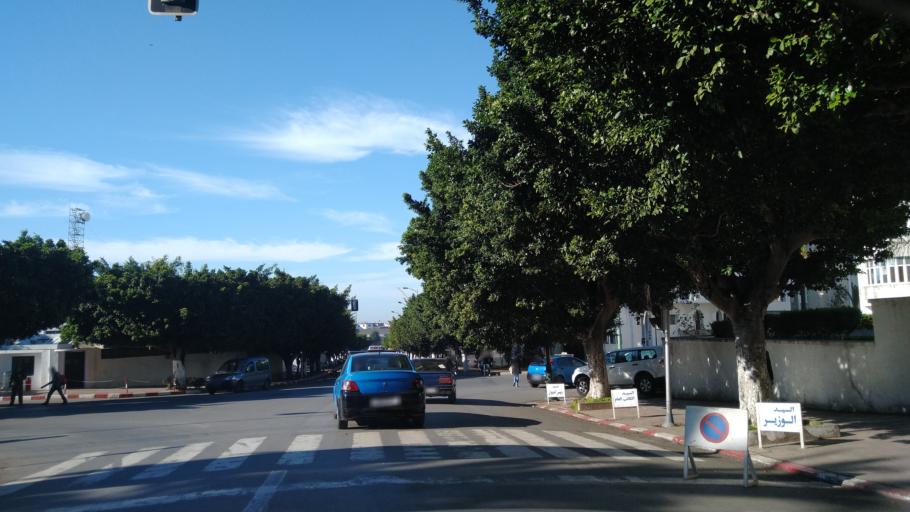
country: MA
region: Rabat-Sale-Zemmour-Zaer
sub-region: Rabat
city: Rabat
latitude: 34.0107
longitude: -6.8285
